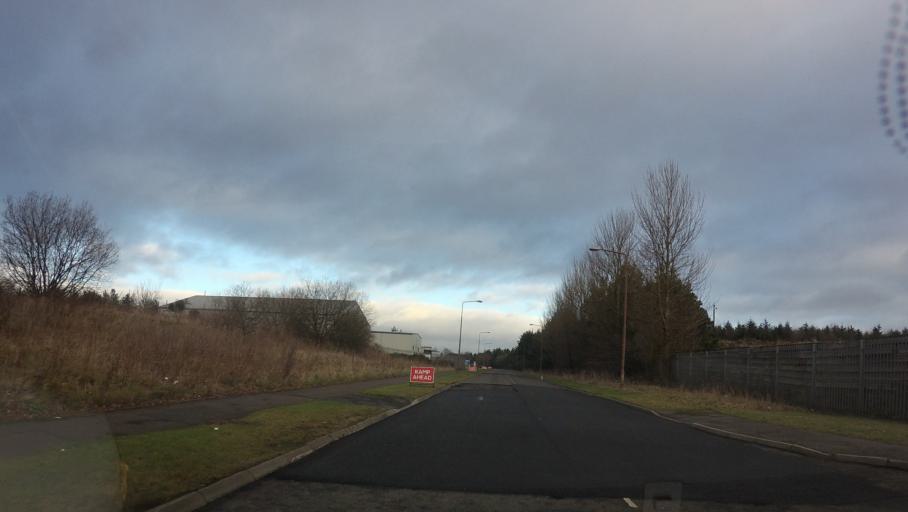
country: GB
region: Scotland
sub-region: West Lothian
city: West Calder
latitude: 55.9018
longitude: -3.5795
